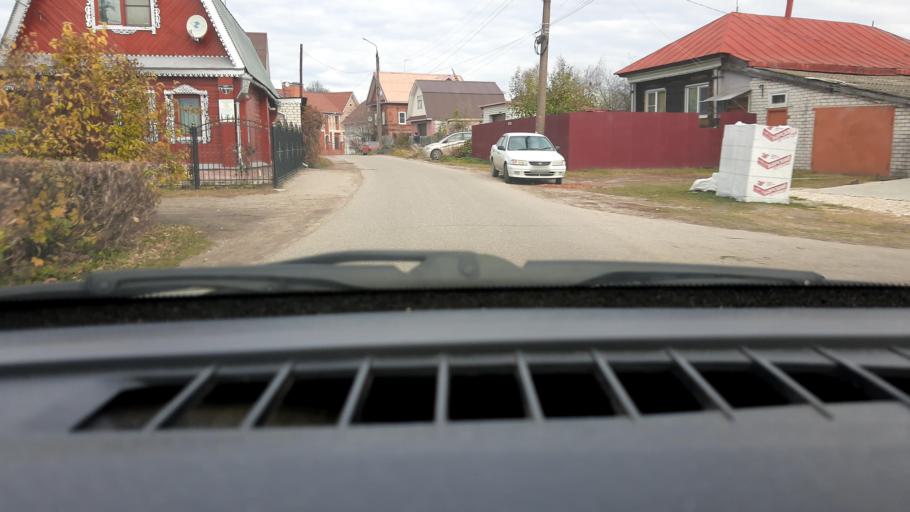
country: RU
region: Nizjnij Novgorod
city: Gorodets
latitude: 56.6399
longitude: 43.4702
